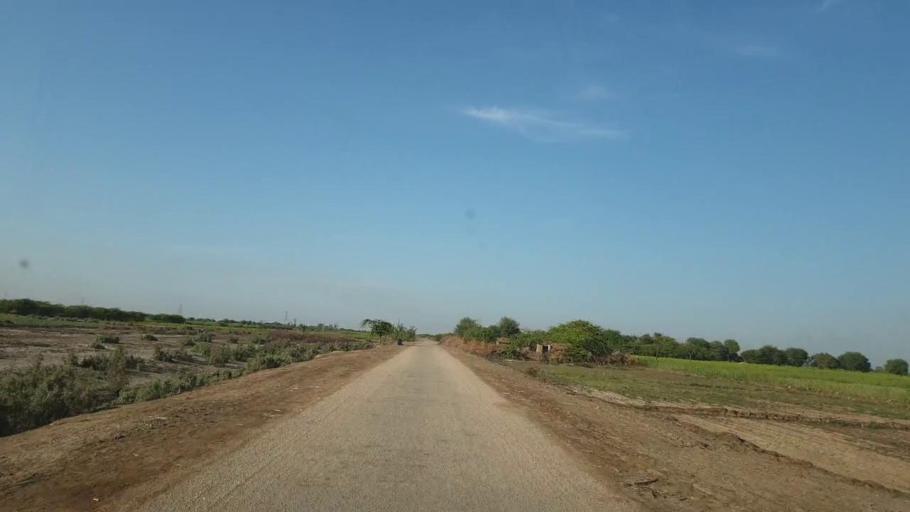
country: PK
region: Sindh
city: Kunri
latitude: 25.0925
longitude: 69.4203
